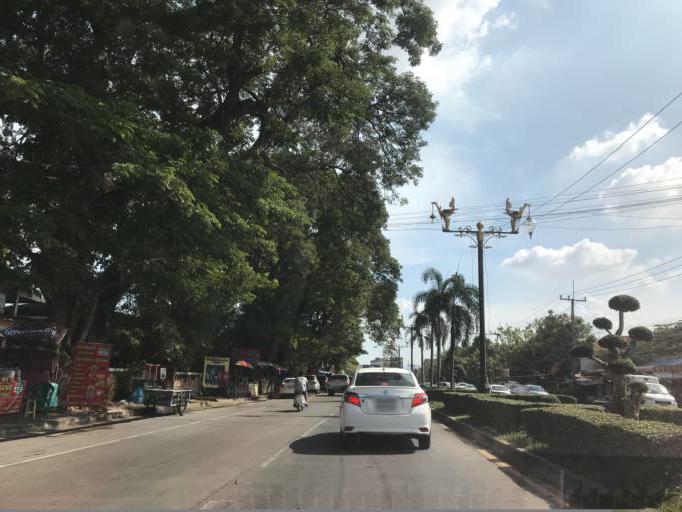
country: TH
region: Phra Nakhon Si Ayutthaya
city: Phra Nakhon Si Ayutthaya
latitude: 14.3460
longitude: 100.5613
